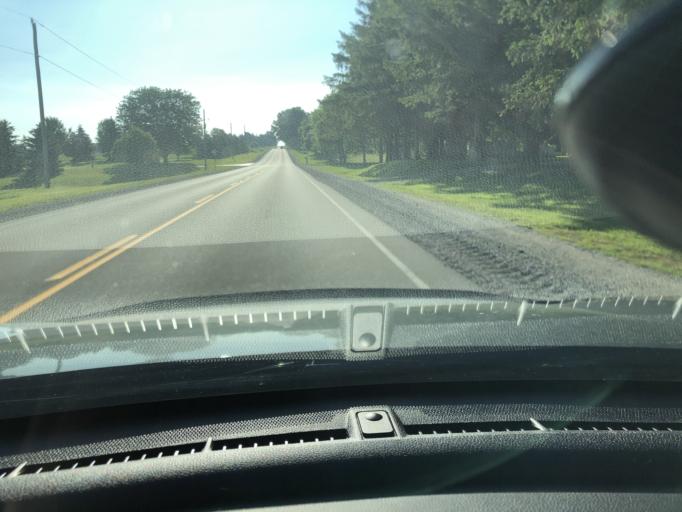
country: CA
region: Ontario
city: Stratford
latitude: 43.4247
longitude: -80.8119
